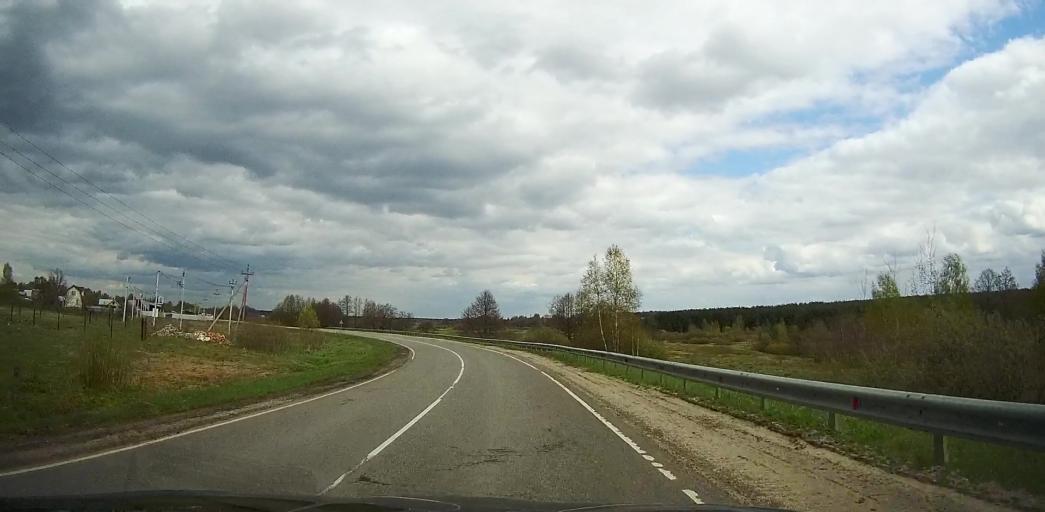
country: RU
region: Moskovskaya
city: Imeni Tsyurupy
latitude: 55.4851
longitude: 38.6188
